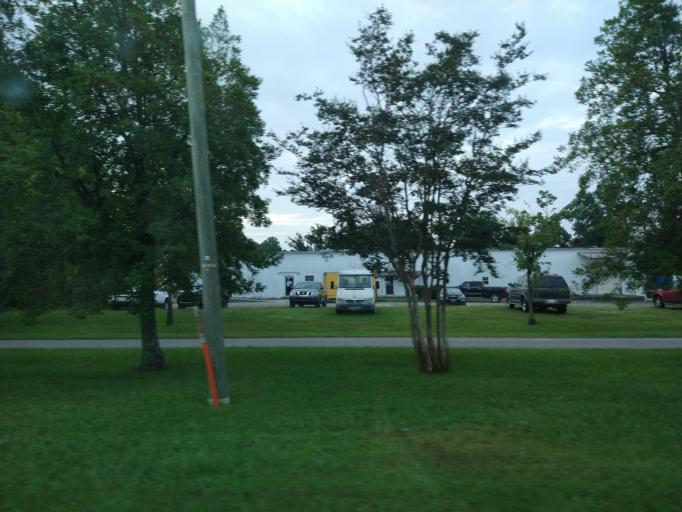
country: US
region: North Carolina
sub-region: Onslow County
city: Jacksonville
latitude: 34.7633
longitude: -77.4122
